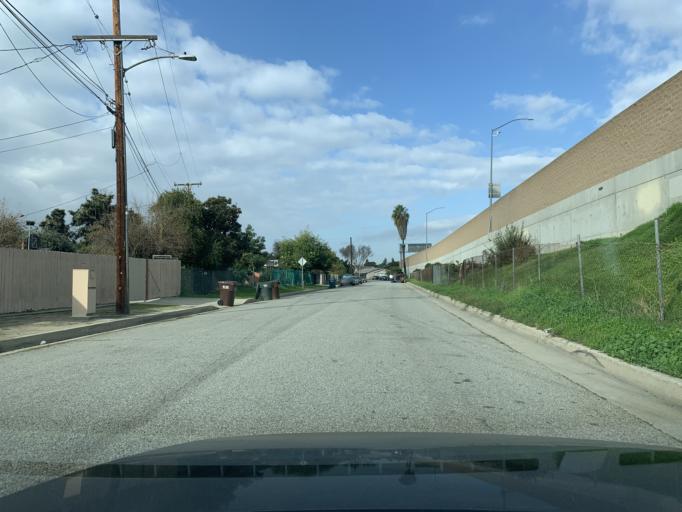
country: US
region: California
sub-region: Los Angeles County
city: El Monte
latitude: 34.0685
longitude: -118.0440
